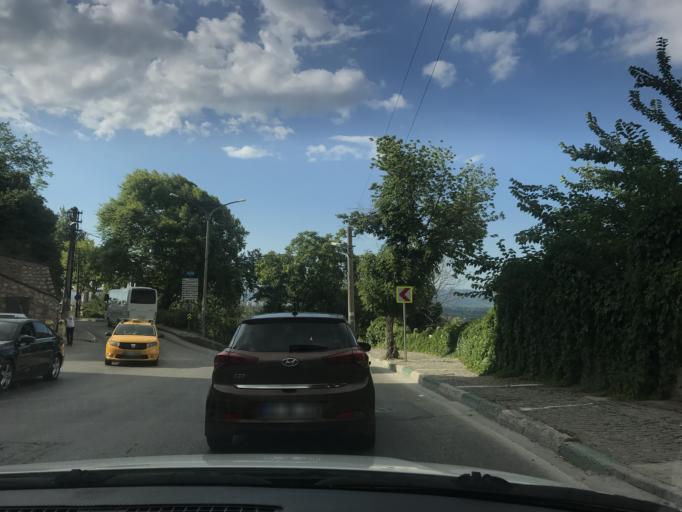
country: TR
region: Bursa
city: Yildirim
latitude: 40.2025
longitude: 29.0229
